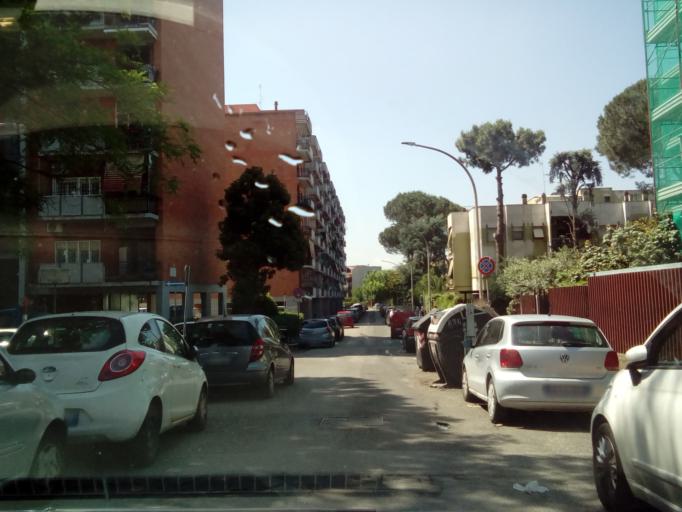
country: IT
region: Latium
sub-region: Citta metropolitana di Roma Capitale
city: Rome
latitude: 41.8879
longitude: 12.5844
